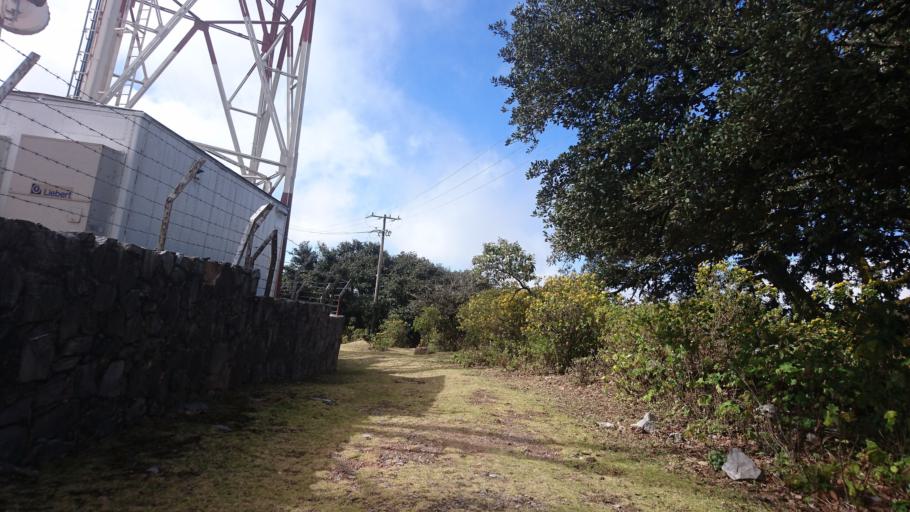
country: MX
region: San Luis Potosi
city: Zaragoza
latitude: 22.0659
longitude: -100.6495
